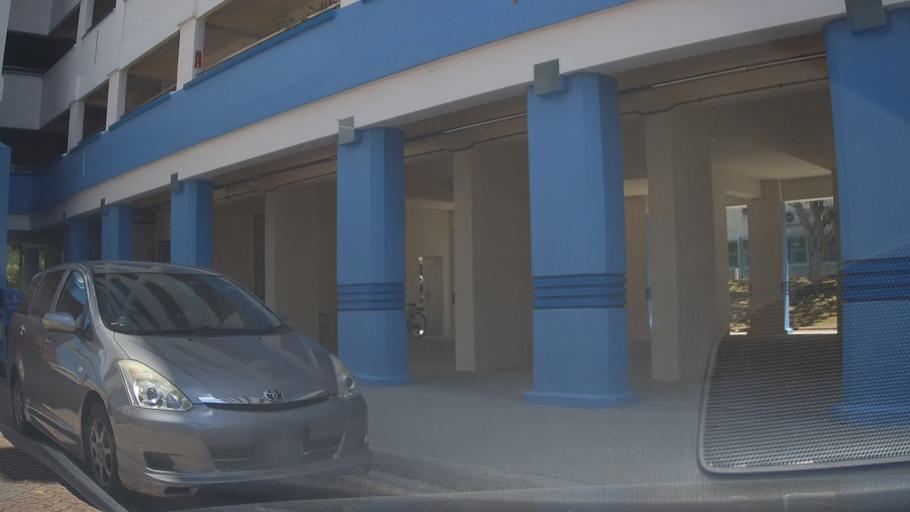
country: MY
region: Johor
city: Kampung Pasir Gudang Baru
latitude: 1.3683
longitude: 103.9642
